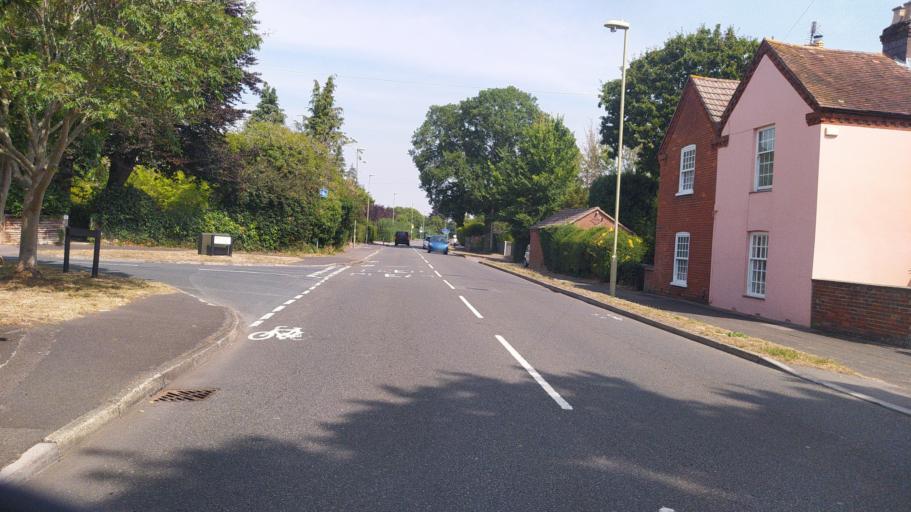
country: GB
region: England
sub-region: Hampshire
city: Havant
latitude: 50.8512
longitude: -0.9687
